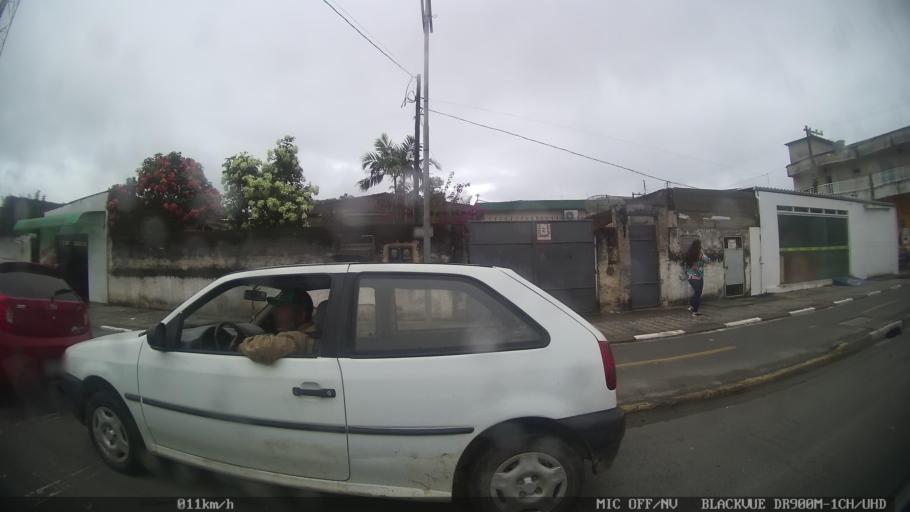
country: BR
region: Sao Paulo
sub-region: Juquia
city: Juquia
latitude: -24.3196
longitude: -47.6359
